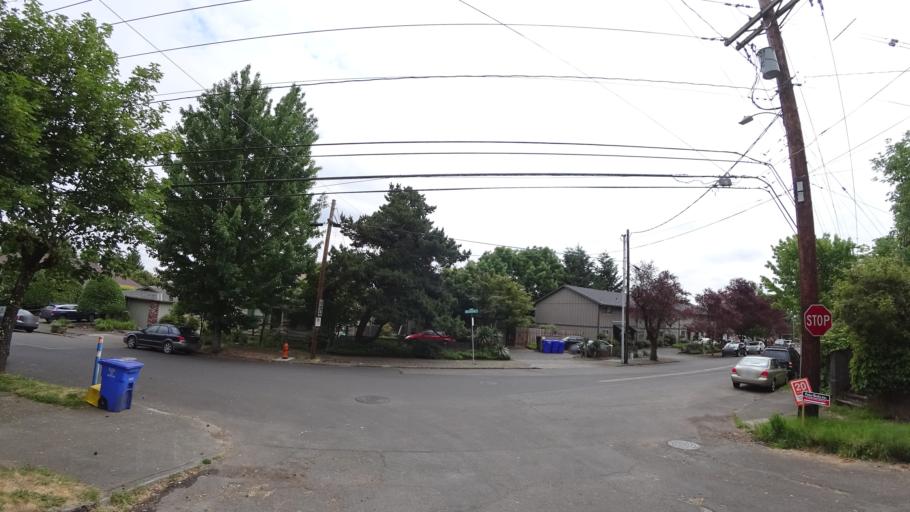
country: US
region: Oregon
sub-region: Clackamas County
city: Milwaukie
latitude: 45.4713
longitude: -122.6738
